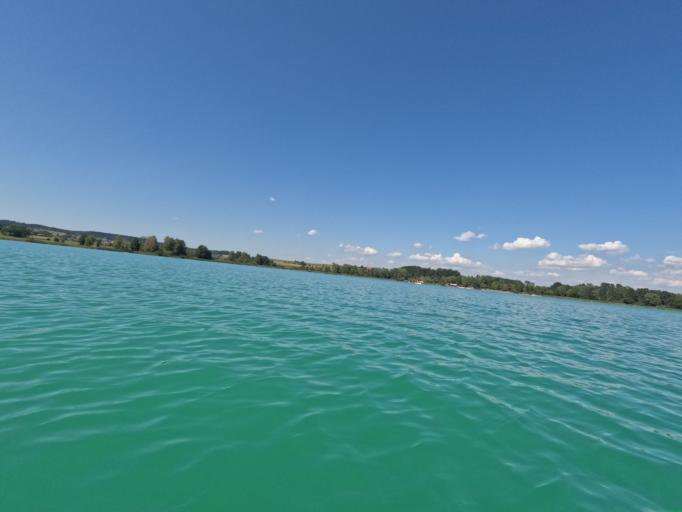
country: DE
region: Bavaria
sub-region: Upper Bavaria
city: Taching am See
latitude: 47.9826
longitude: 12.7446
